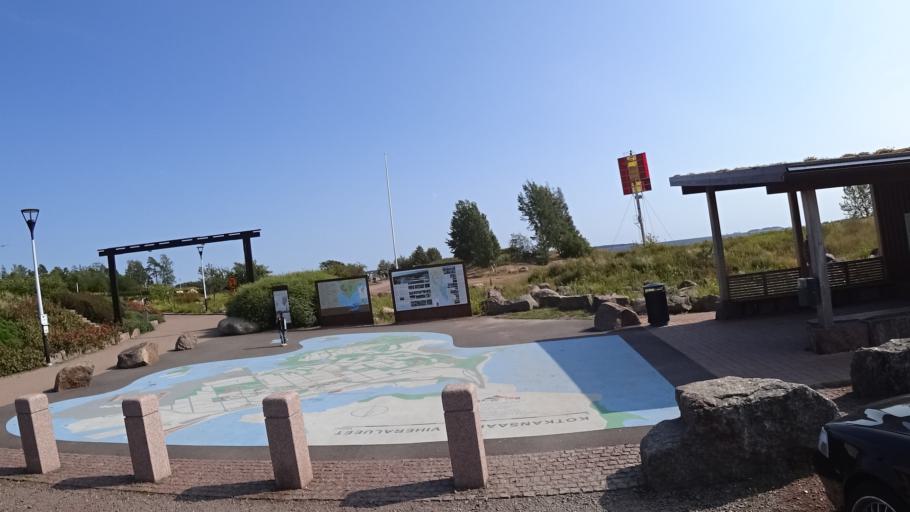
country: FI
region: Kymenlaakso
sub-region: Kotka-Hamina
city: Kotka
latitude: 60.4479
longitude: 26.9359
